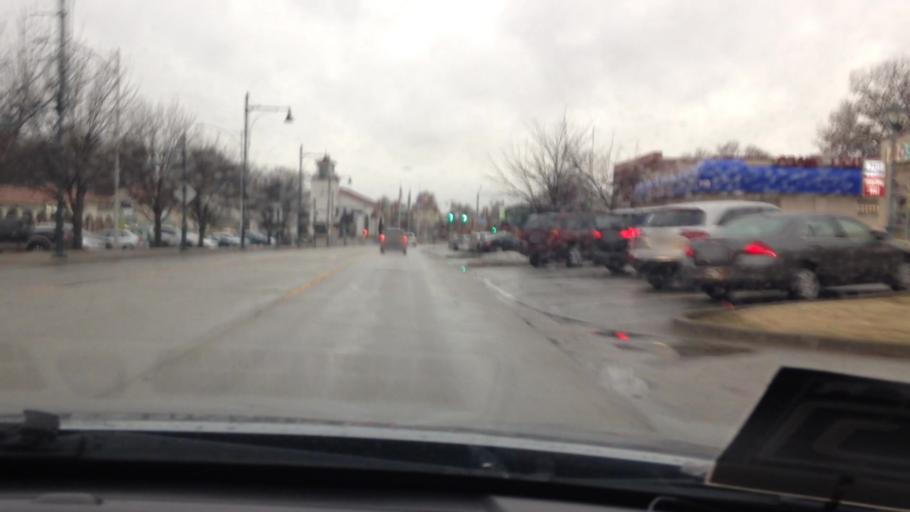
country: US
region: Kansas
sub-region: Johnson County
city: Mission
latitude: 39.0229
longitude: -94.6473
